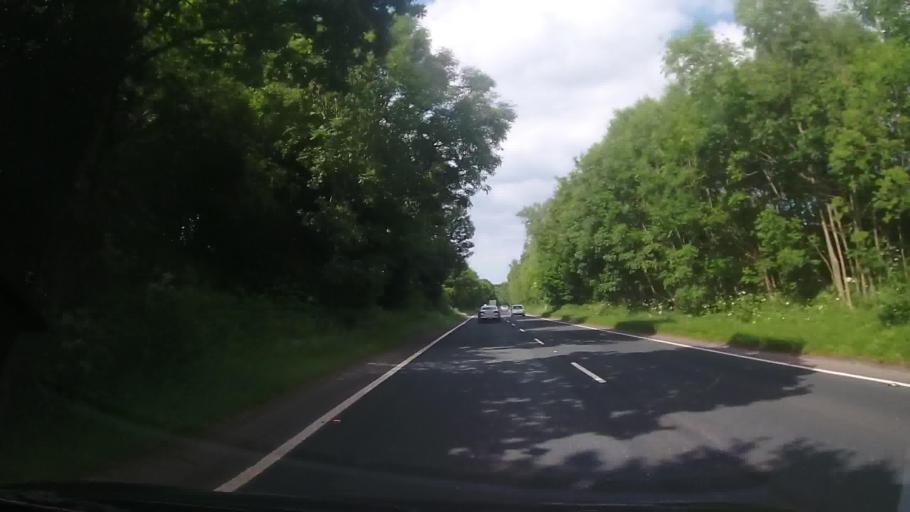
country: GB
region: England
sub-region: Shropshire
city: Ludlow
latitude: 52.3467
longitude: -2.7096
